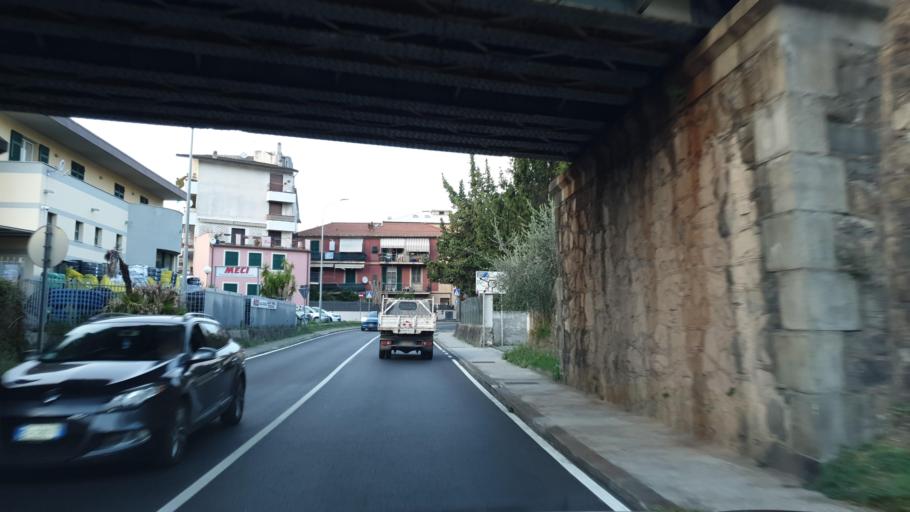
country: IT
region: Liguria
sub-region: Provincia di Genova
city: Sestri Levante
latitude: 44.2693
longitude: 9.4164
